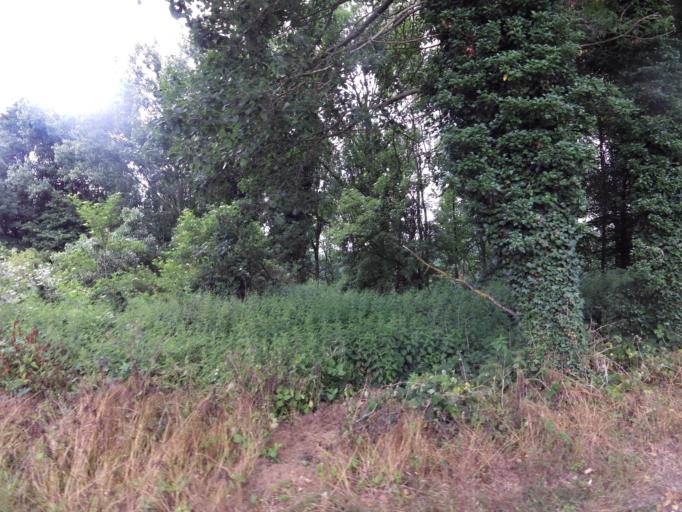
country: FR
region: Nord-Pas-de-Calais
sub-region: Departement du Nord
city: Steenwerck
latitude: 50.7733
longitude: 2.8034
